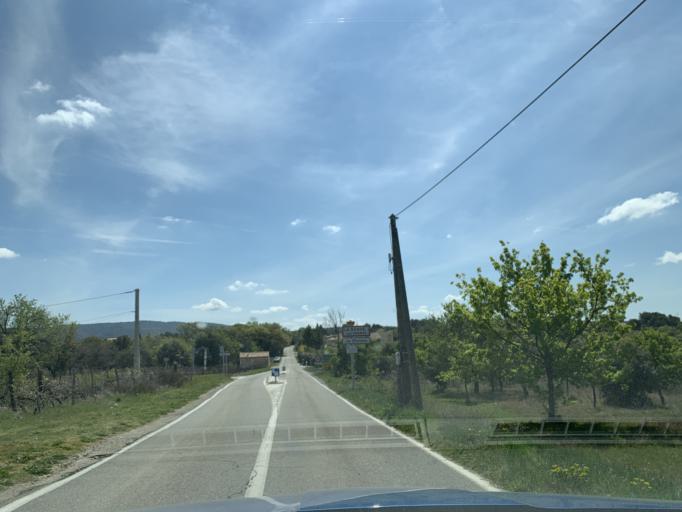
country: FR
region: Provence-Alpes-Cote d'Azur
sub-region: Departement du Vaucluse
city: Saint-Didier
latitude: 43.9869
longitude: 5.1089
